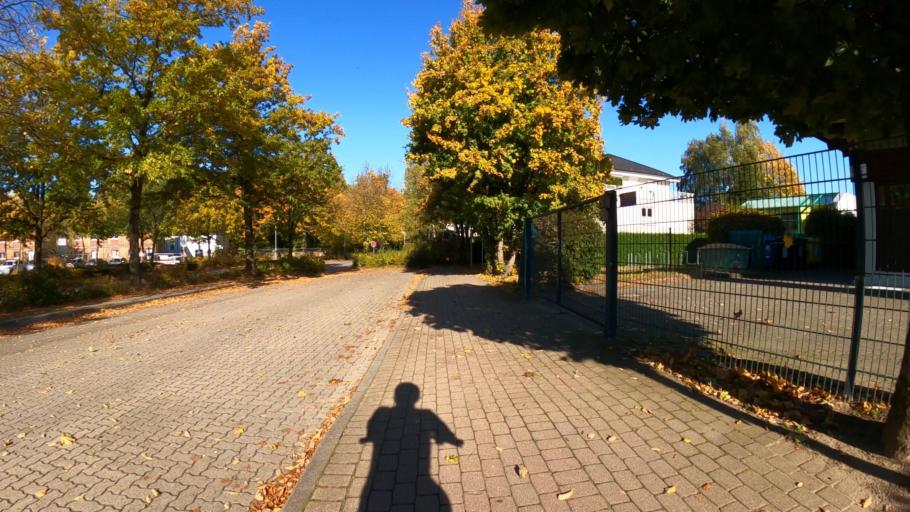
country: DE
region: Schleswig-Holstein
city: Ahrensburg
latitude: 53.6814
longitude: 10.2343
